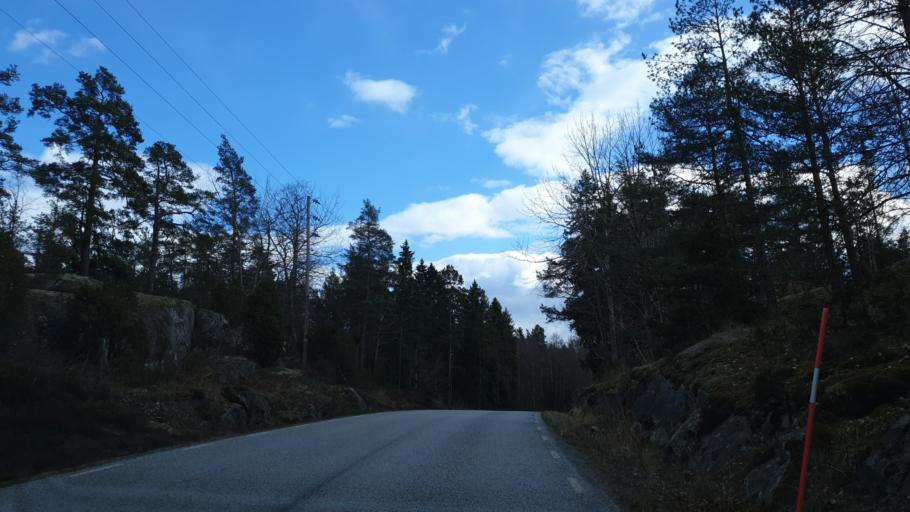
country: SE
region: Stockholm
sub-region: Varmdo Kommun
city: Hemmesta
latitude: 59.2304
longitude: 18.4842
